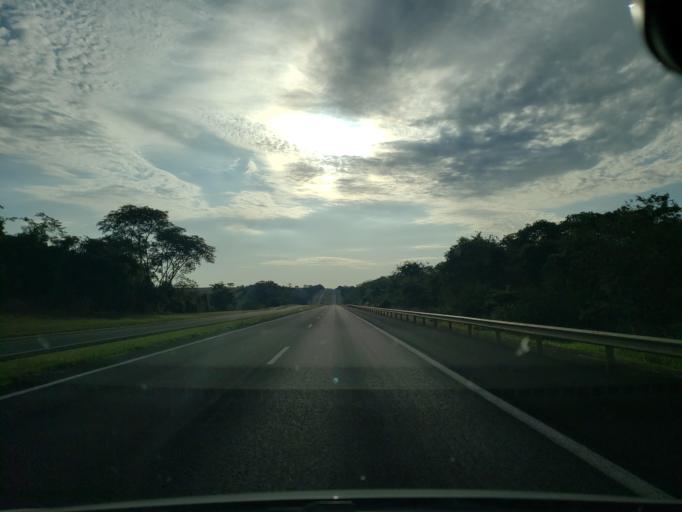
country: BR
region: Sao Paulo
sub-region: Mirandopolis
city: Mirandopolis
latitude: -21.1026
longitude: -51.0368
